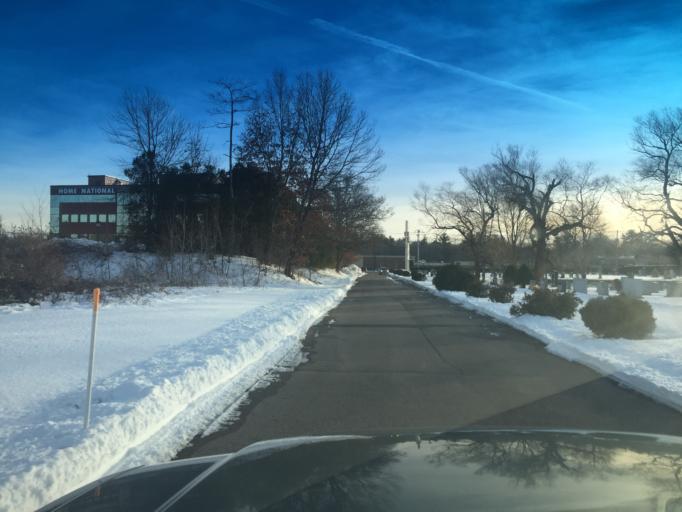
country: US
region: Massachusetts
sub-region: Worcester County
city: Milford
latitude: 42.1495
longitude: -71.4903
